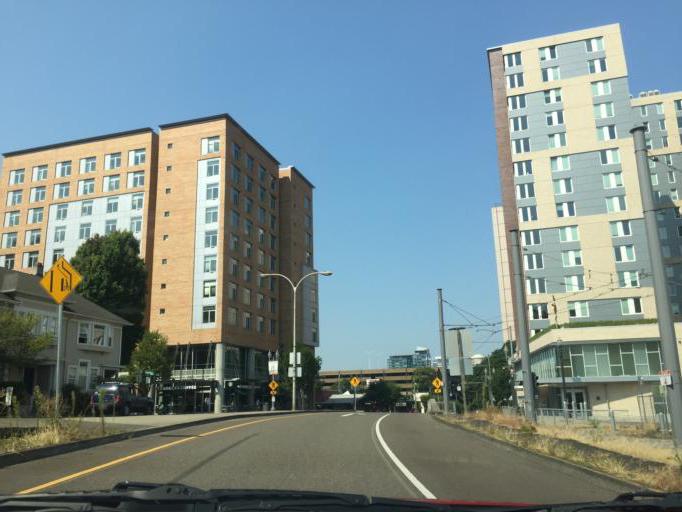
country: US
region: Oregon
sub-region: Multnomah County
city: Portland
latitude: 45.5086
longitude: -122.6840
